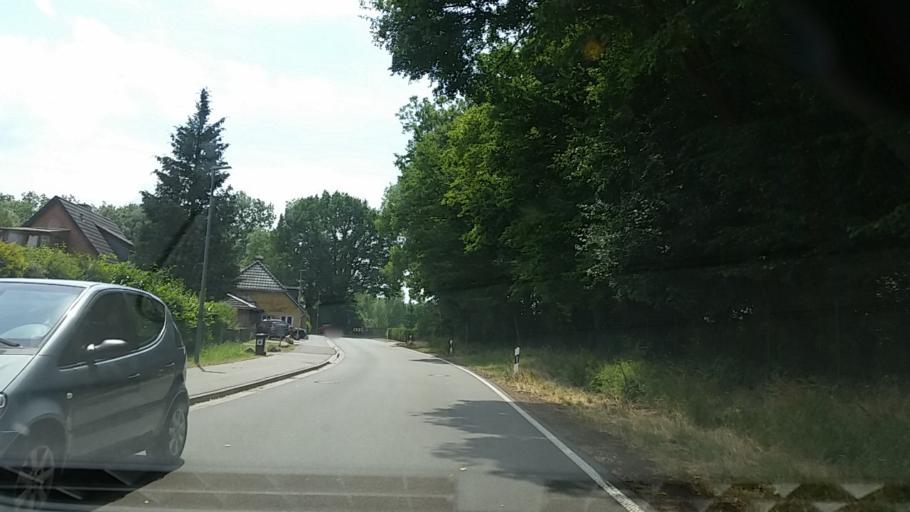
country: DE
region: Schleswig-Holstein
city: Tremsbuttel
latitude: 53.7423
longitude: 10.3153
